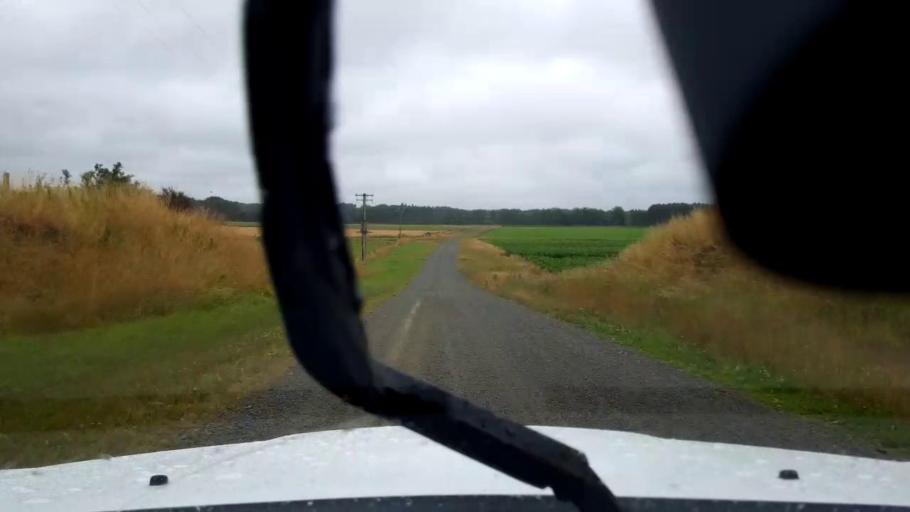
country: NZ
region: Canterbury
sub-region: Timaru District
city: Pleasant Point
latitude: -44.2514
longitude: 171.2004
